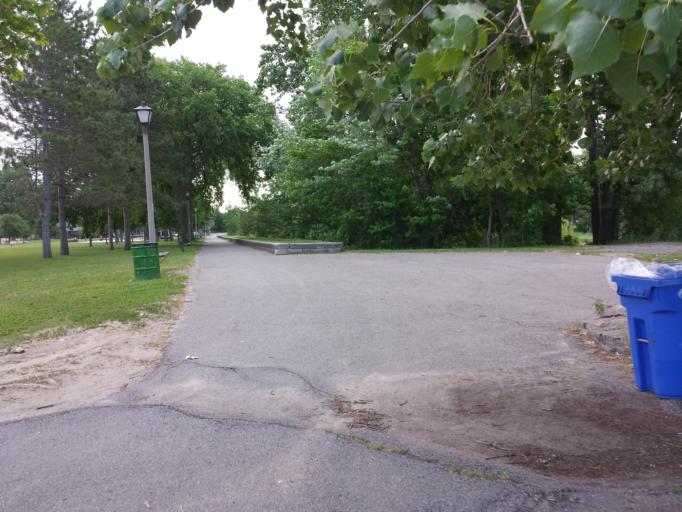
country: CA
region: Ontario
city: Bells Corners
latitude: 45.3645
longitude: -75.8055
